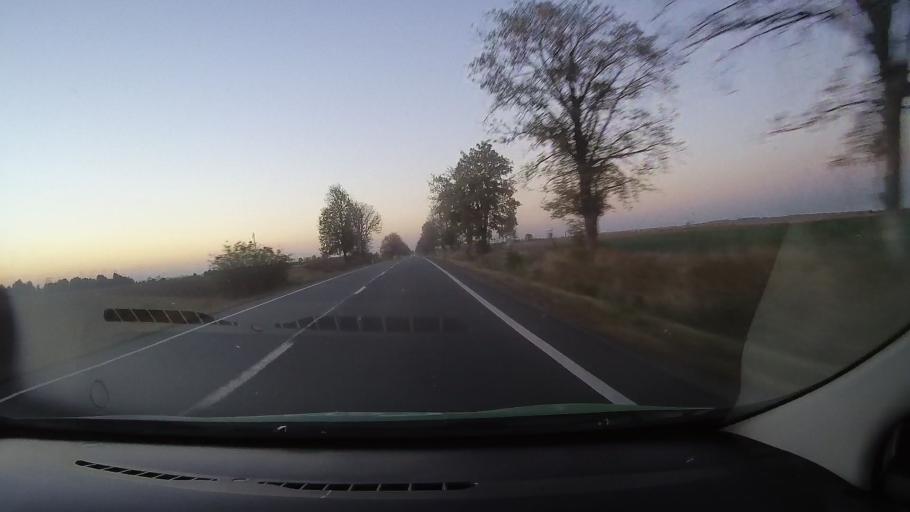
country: RO
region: Bihor
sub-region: Comuna Valea lui Mihai
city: Valea lui Mihai
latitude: 47.4947
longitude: 22.1523
